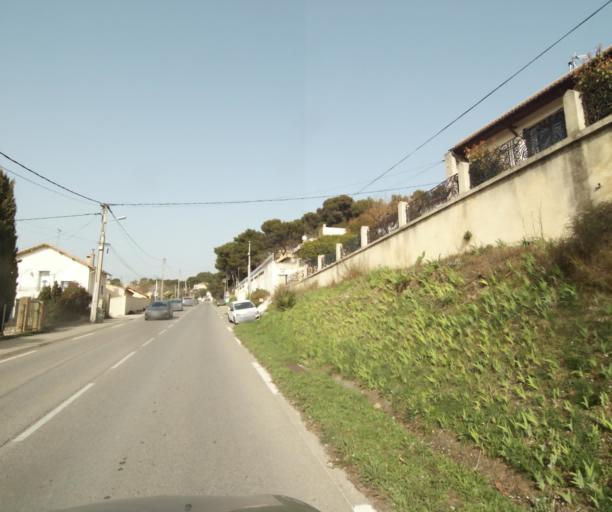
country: FR
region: Provence-Alpes-Cote d'Azur
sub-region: Departement des Bouches-du-Rhone
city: Marseille 15
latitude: 43.3917
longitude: 5.3439
